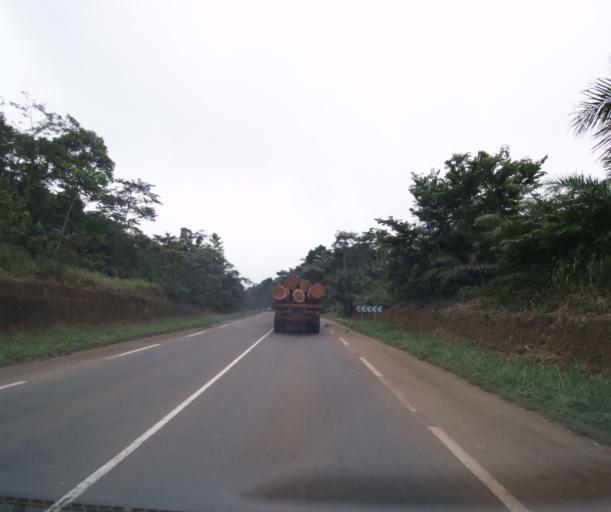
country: CM
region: Centre
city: Mbankomo
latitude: 3.7660
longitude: 11.1267
